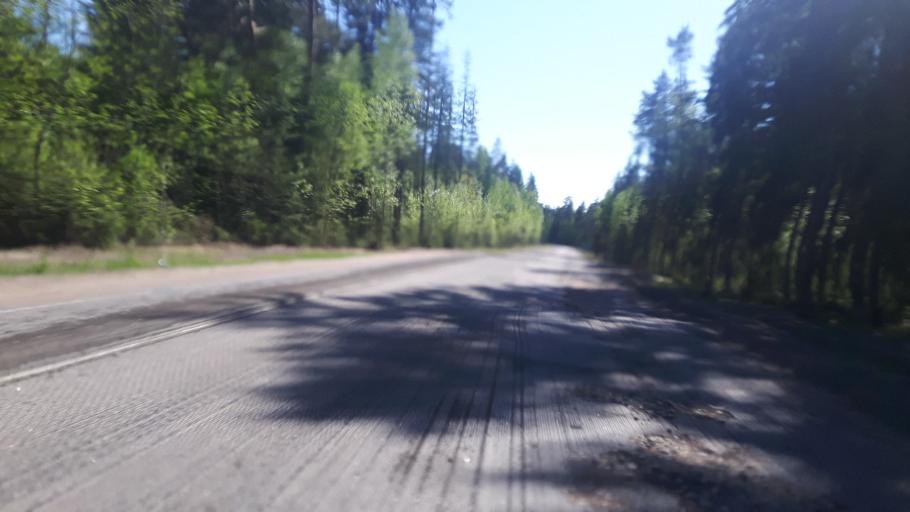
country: RU
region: Leningrad
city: Sosnovyy Bor
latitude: 60.2369
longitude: 29.0028
